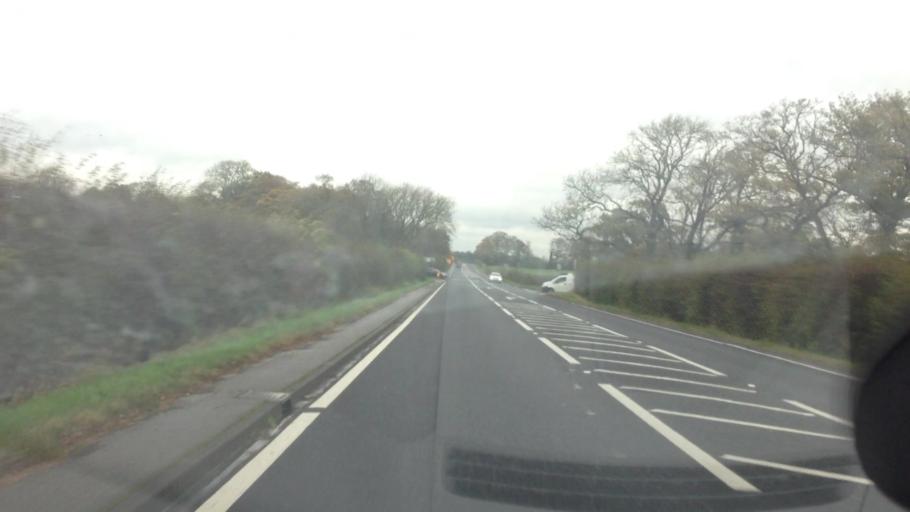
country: GB
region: England
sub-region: City and Borough of Leeds
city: Shadwell
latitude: 53.8487
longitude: -1.4649
